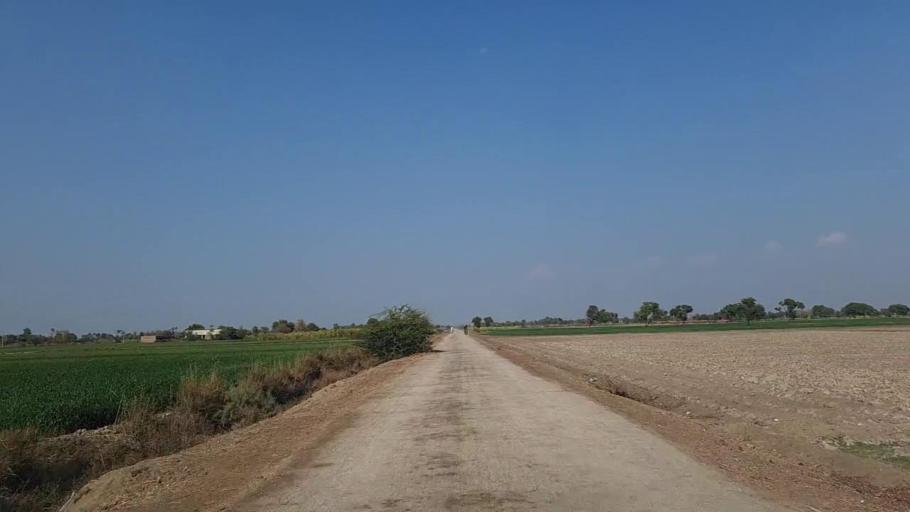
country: PK
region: Sindh
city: Jam Sahib
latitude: 26.2848
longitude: 68.5830
